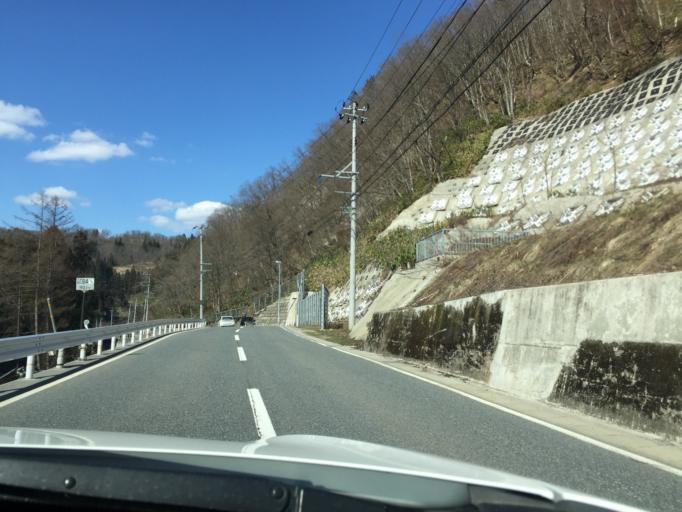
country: JP
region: Yamagata
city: Nagai
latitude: 38.2427
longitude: 140.0946
